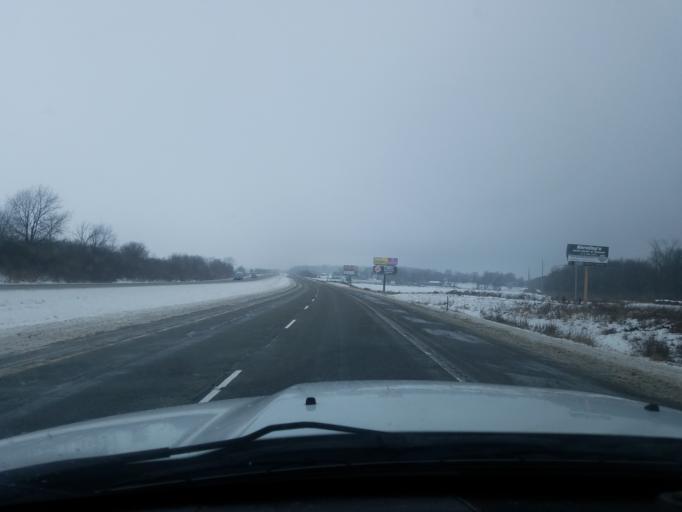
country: US
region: Indiana
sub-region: Fulton County
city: Rochester
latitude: 41.0303
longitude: -86.1834
